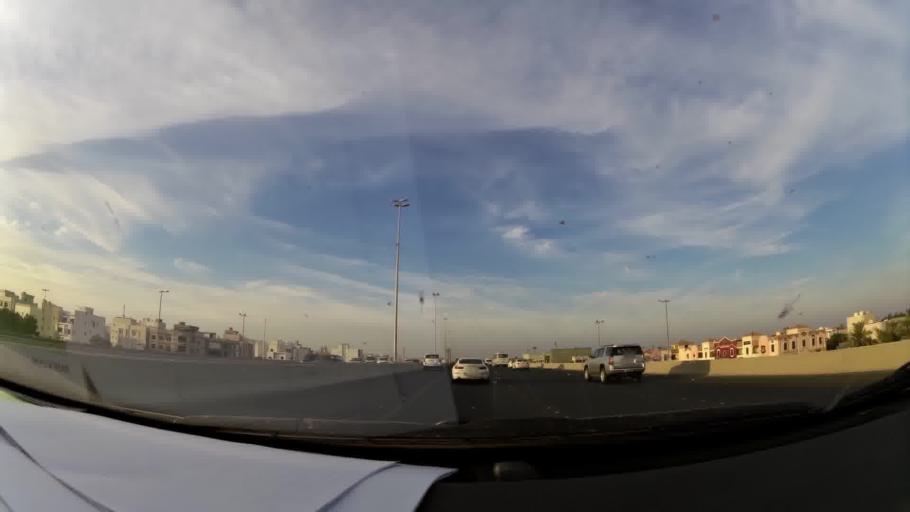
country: KW
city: Al Funaytis
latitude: 29.2122
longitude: 48.1034
